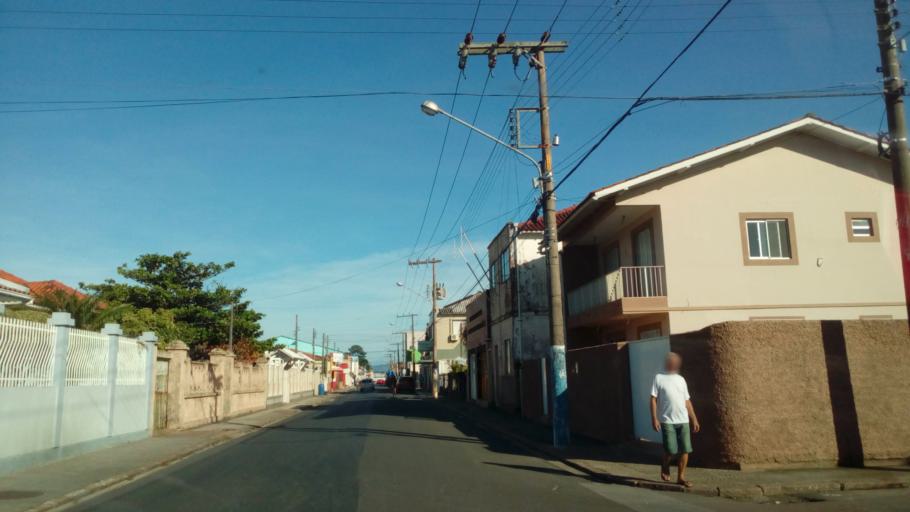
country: BR
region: Santa Catarina
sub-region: Laguna
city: Laguna
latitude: -28.4922
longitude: -48.7818
